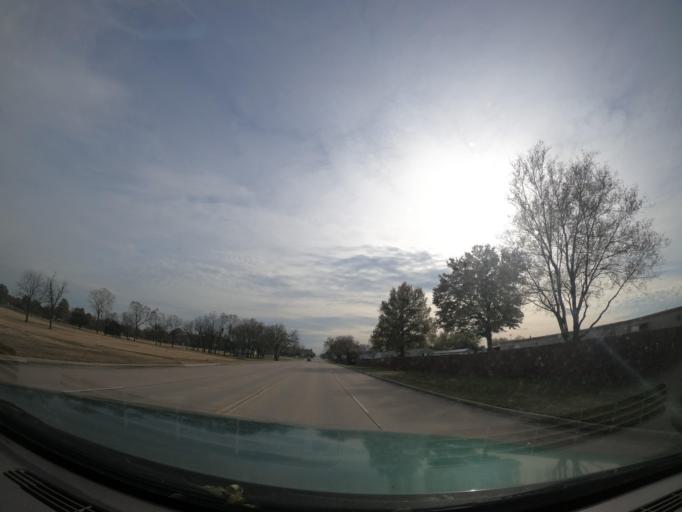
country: US
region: Oklahoma
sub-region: Tulsa County
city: Turley
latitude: 36.2462
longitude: -95.9584
